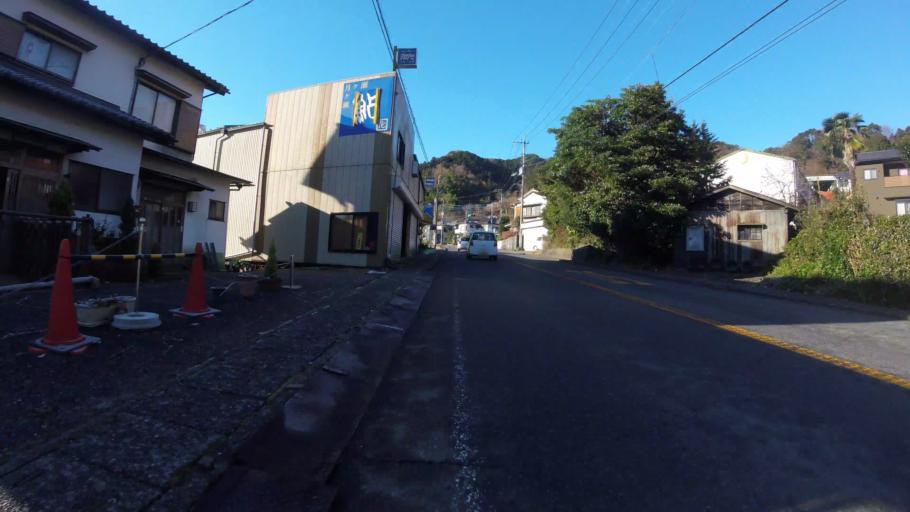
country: JP
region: Shizuoka
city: Heda
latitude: 34.9198
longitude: 138.9252
